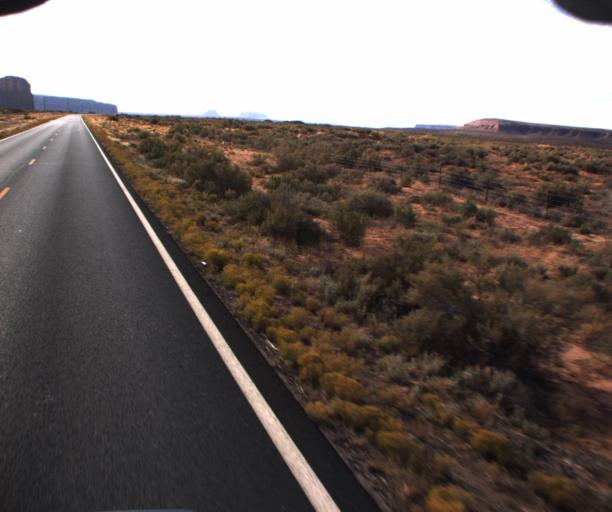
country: US
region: Arizona
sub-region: Apache County
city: Many Farms
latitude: 36.6859
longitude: -109.6066
